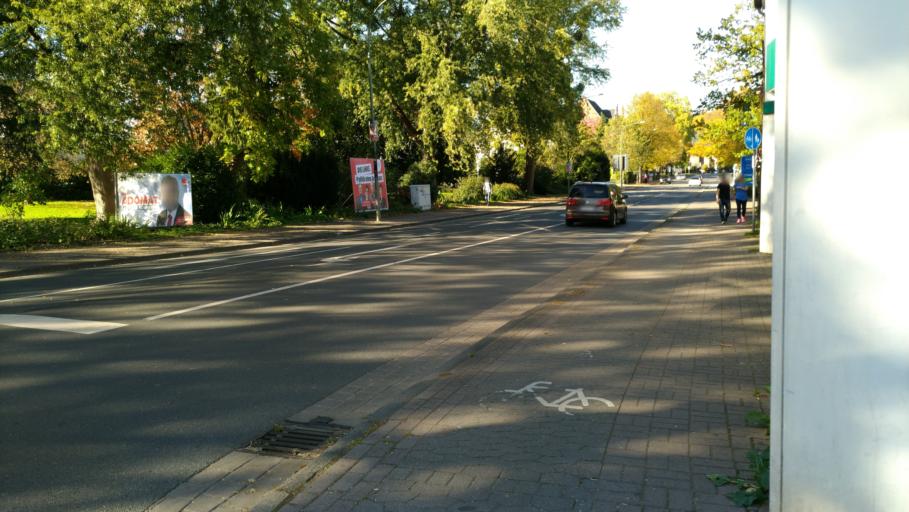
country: DE
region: Lower Saxony
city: Rinteln
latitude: 52.1937
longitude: 9.0817
